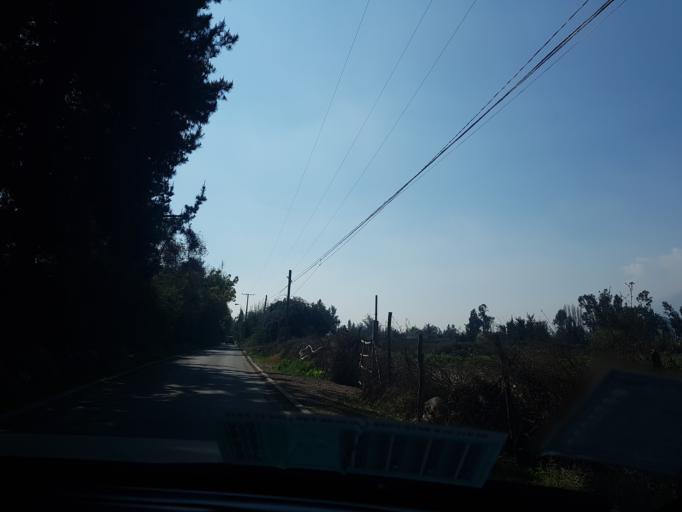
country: CL
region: Santiago Metropolitan
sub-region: Provincia de Cordillera
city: Puente Alto
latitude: -33.6291
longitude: -70.5598
